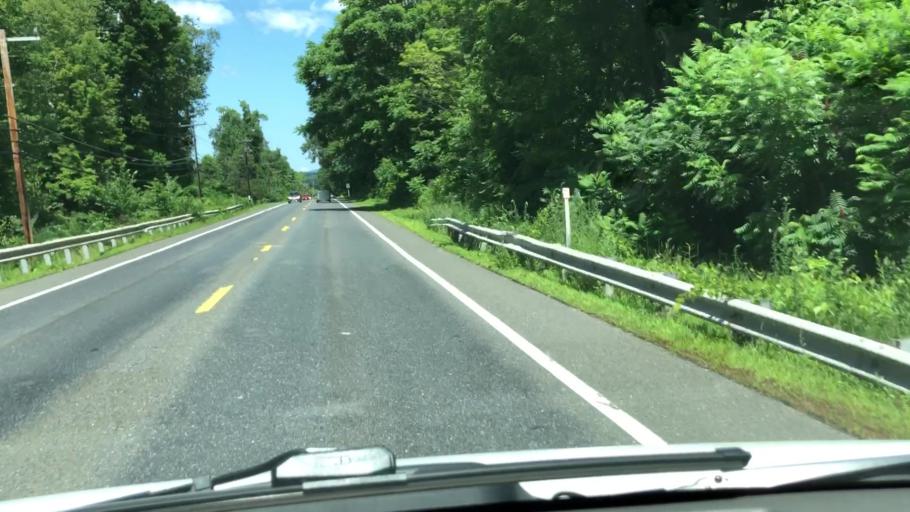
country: US
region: Massachusetts
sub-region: Franklin County
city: Greenfield
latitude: 42.5468
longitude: -72.6010
